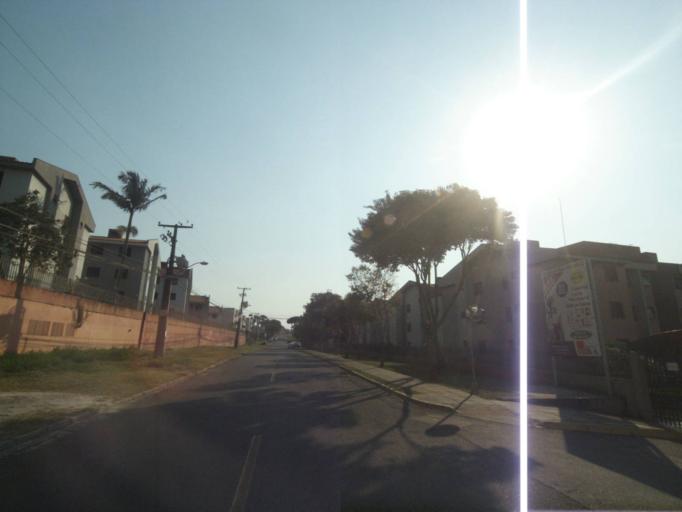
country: BR
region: Parana
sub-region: Curitiba
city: Curitiba
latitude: -25.4931
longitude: -49.2639
